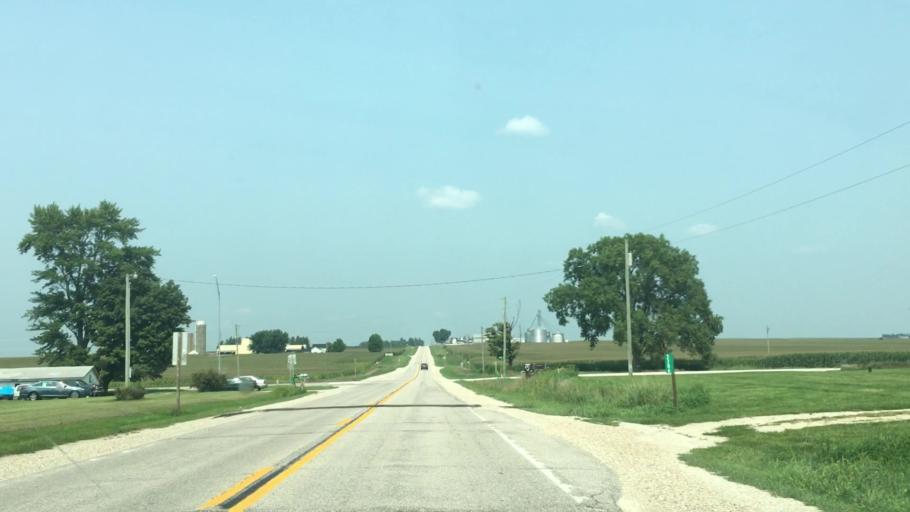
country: US
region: Iowa
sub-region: Benton County
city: Urbana
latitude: 42.3117
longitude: -91.8894
